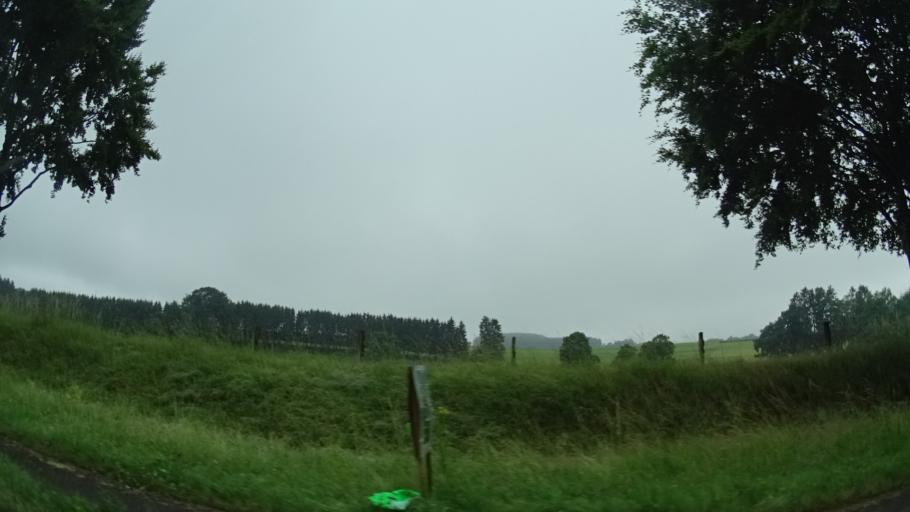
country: BE
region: Wallonia
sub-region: Province du Luxembourg
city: Neufchateau
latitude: 49.8893
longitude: 5.3944
